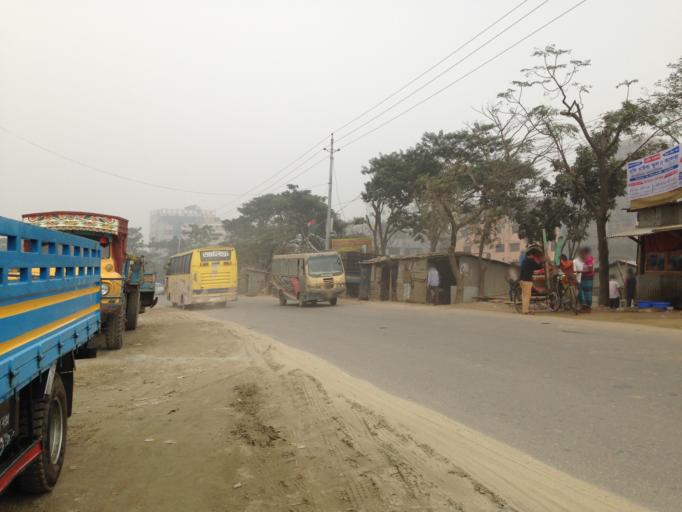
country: BD
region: Dhaka
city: Azimpur
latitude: 23.8004
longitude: 90.3440
